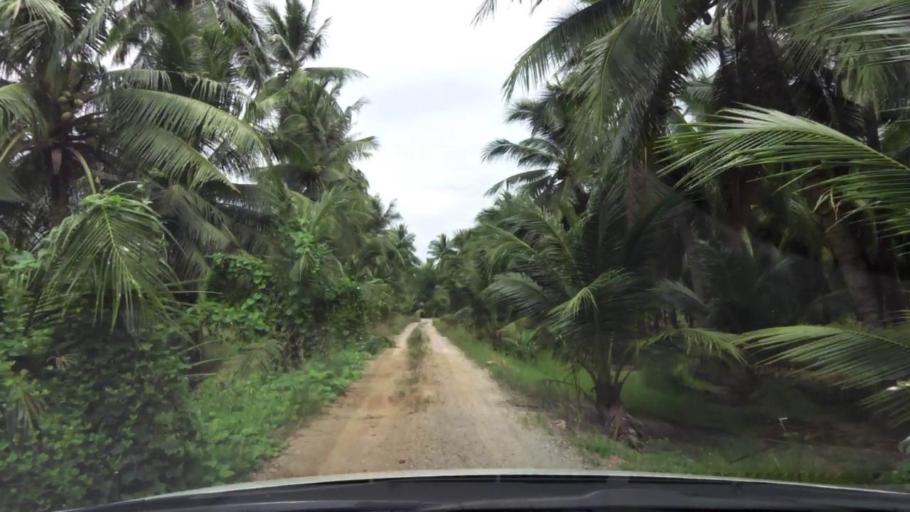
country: TH
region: Ratchaburi
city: Damnoen Saduak
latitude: 13.5532
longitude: 99.9937
